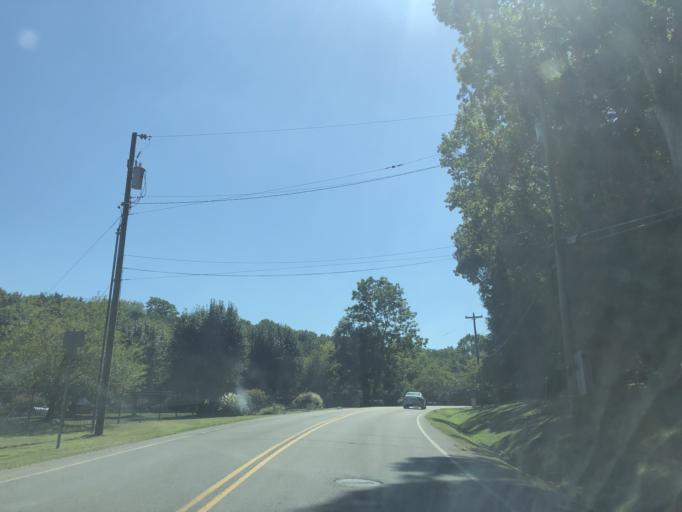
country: US
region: Tennessee
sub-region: Davidson County
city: Forest Hills
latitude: 36.0677
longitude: -86.8436
